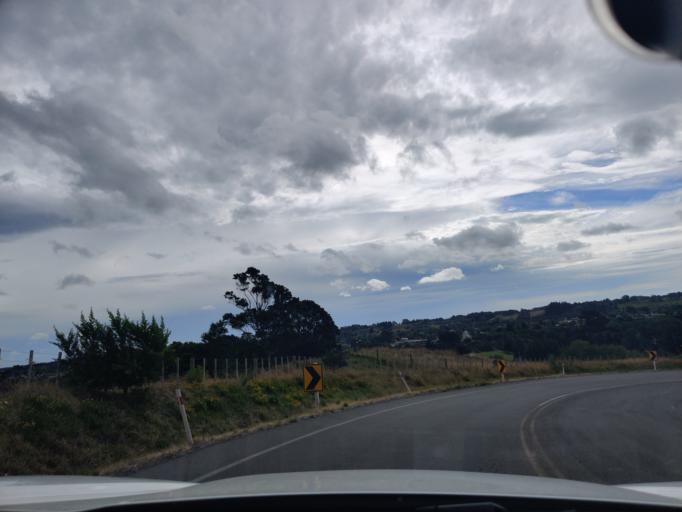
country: NZ
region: Manawatu-Wanganui
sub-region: Palmerston North City
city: Palmerston North
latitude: -40.2860
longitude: 175.7721
